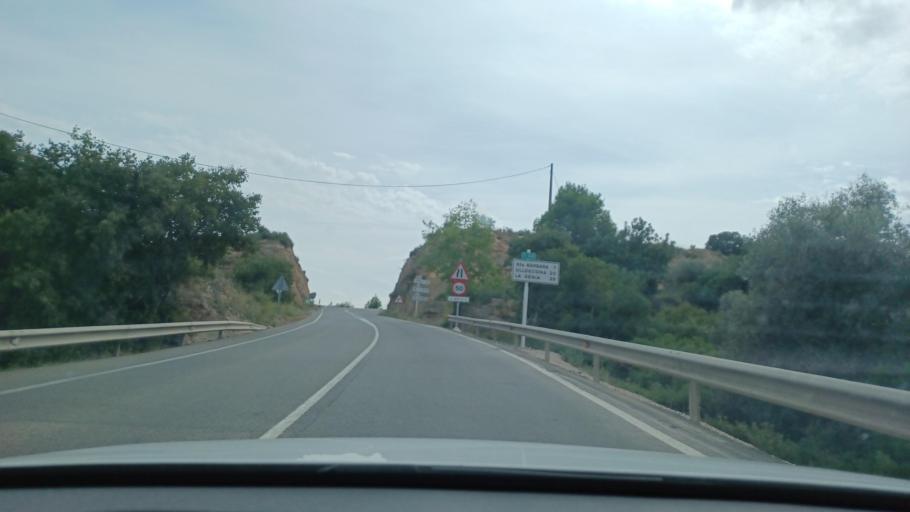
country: ES
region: Catalonia
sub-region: Provincia de Tarragona
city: Tortosa
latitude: 40.7747
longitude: 0.5124
